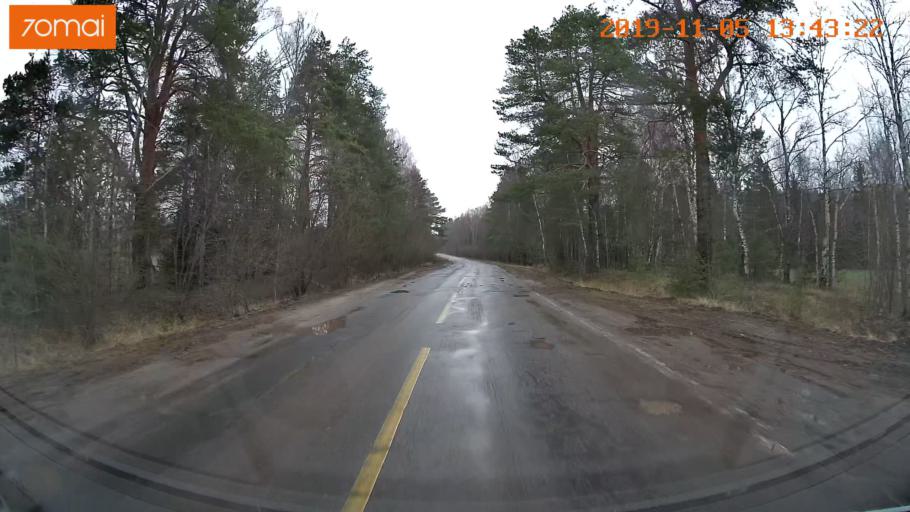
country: RU
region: Ivanovo
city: Shuya
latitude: 56.9731
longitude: 41.4023
